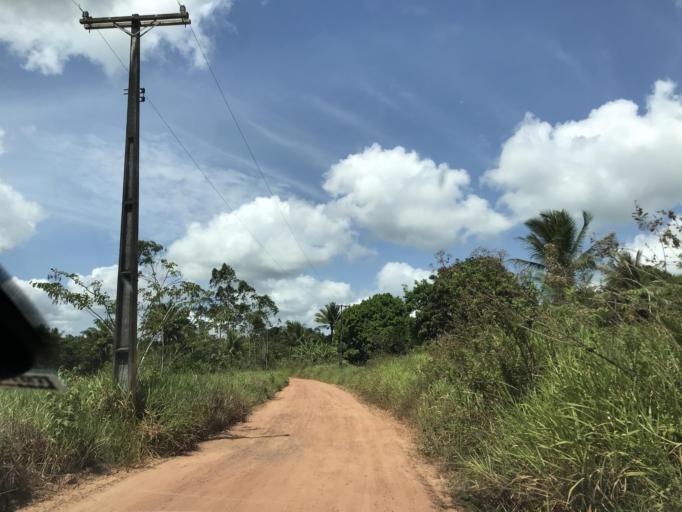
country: BR
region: Bahia
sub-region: Entre Rios
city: Entre Rios
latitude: -12.2222
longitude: -38.0869
